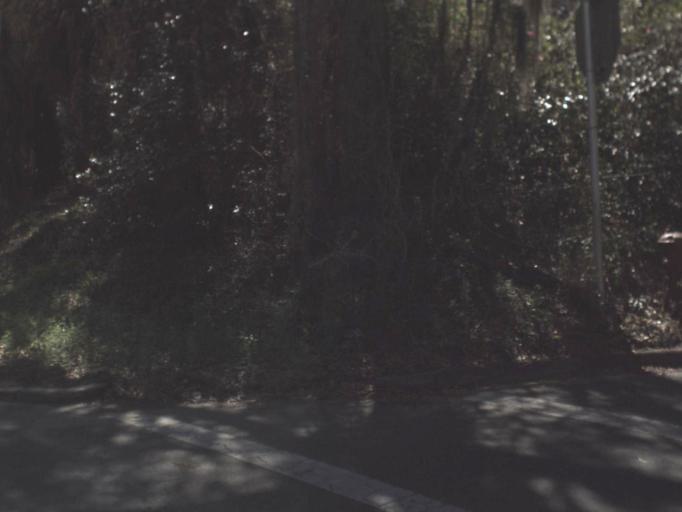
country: US
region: Florida
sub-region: Gadsden County
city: Quincy
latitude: 30.5943
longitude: -84.5780
